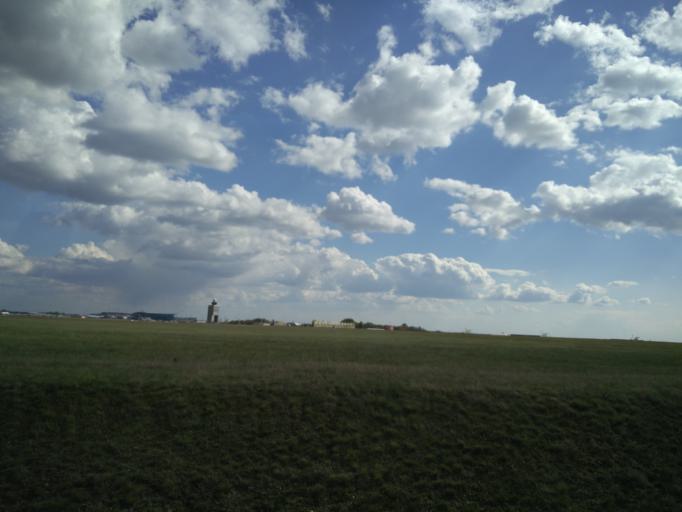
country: HU
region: Budapest
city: Budapest XVII. keruelet
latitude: 47.4500
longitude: 19.2543
